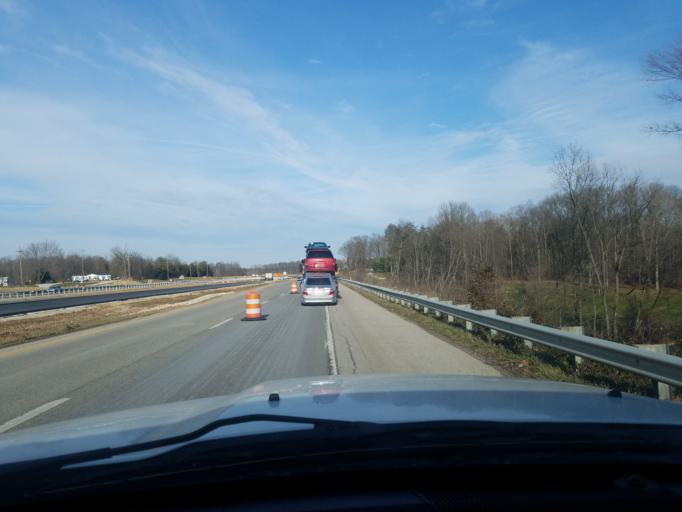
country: US
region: Indiana
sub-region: Monroe County
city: Ellettsville
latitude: 39.2832
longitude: -86.5216
